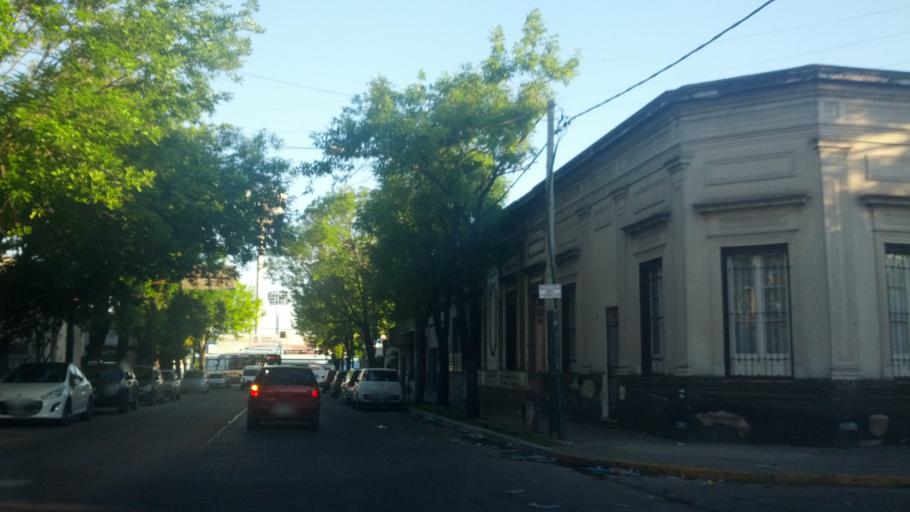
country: AR
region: Buenos Aires
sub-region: Partido de Lomas de Zamora
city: Lomas de Zamora
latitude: -34.7812
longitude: -58.4010
